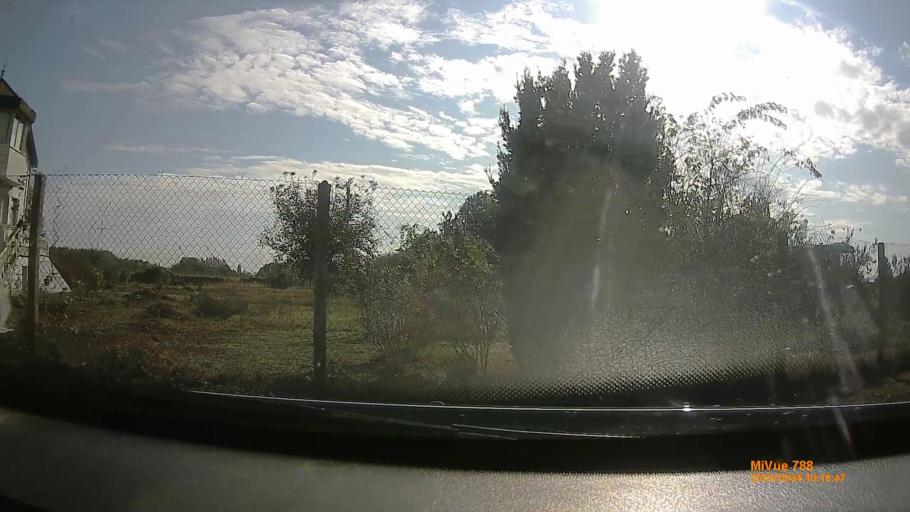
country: HU
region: Szabolcs-Szatmar-Bereg
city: Nyiregyhaza
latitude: 47.9603
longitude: 21.6574
